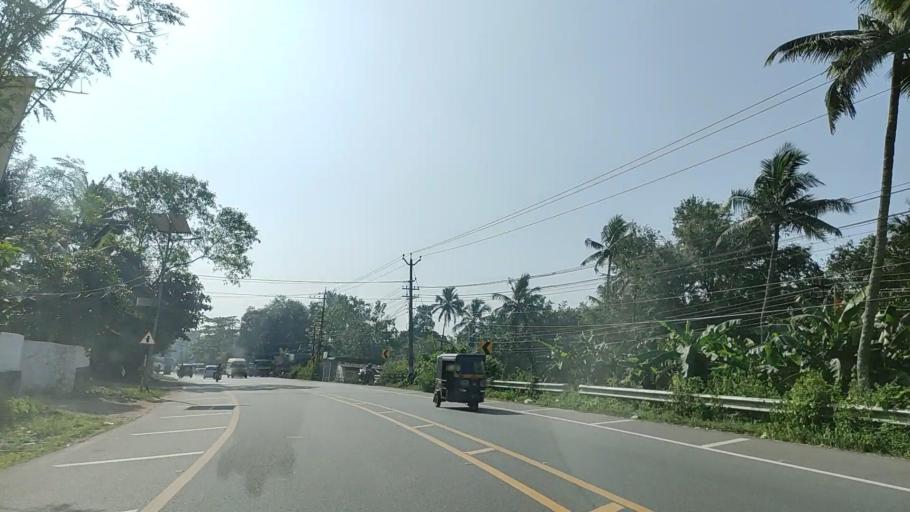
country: IN
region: Kerala
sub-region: Kollam
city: Punalur
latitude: 8.8777
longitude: 76.8669
